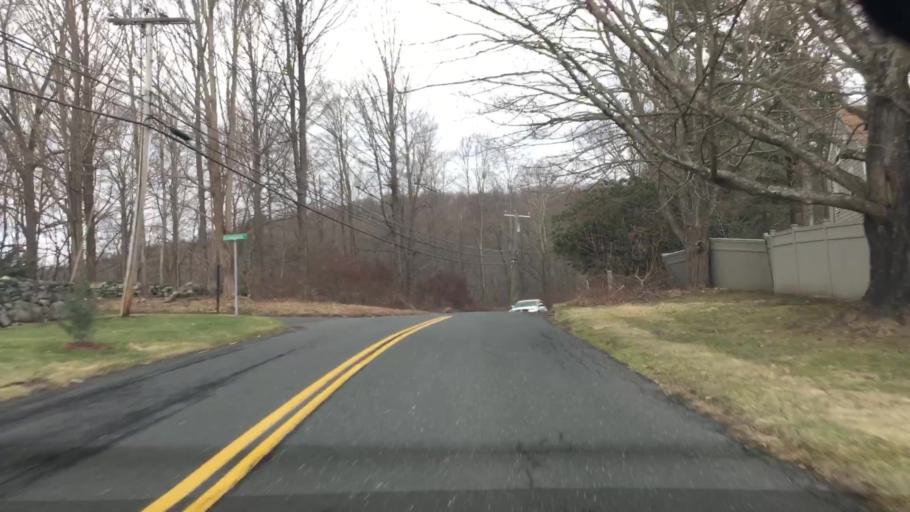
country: US
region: New York
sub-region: Putnam County
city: Peach Lake
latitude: 41.3726
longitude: -73.5277
